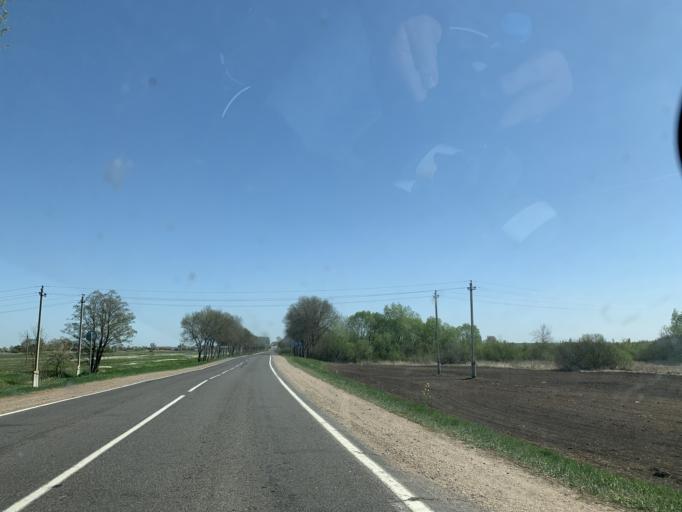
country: BY
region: Minsk
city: Nyasvizh
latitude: 53.2300
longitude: 26.7332
